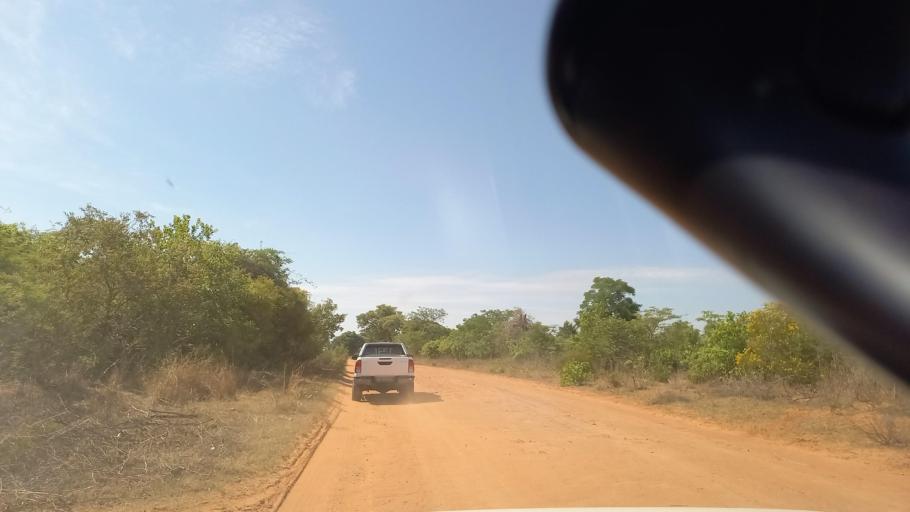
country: ZM
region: Southern
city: Mazabuka
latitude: -16.0360
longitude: 27.6176
